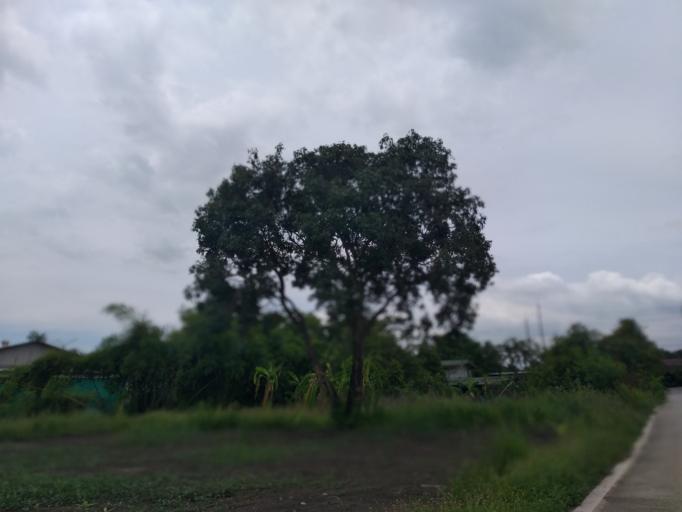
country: TH
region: Pathum Thani
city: Ban Lam Luk Ka
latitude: 13.9585
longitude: 100.8528
